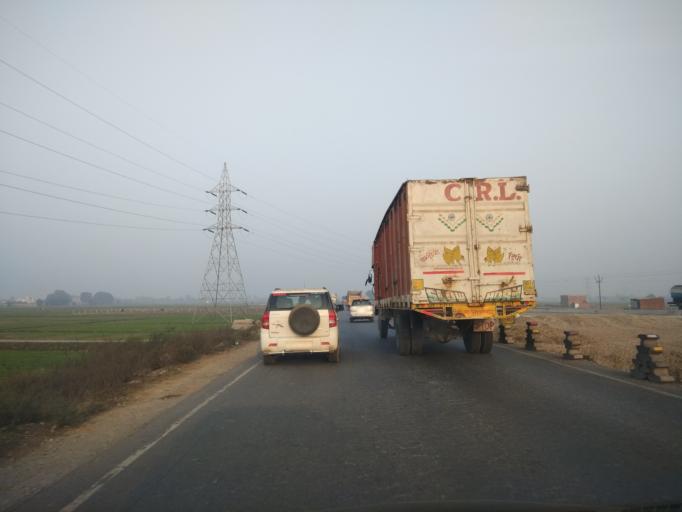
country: IN
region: Uttar Pradesh
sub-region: Chandauli District
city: Mughal Sarai
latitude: 25.2623
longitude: 83.1392
